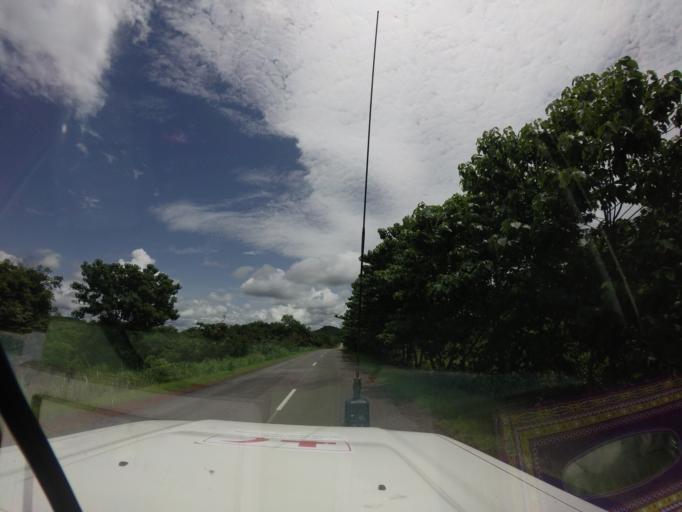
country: SL
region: Northern Province
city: Gberia Fotombu
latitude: 10.0604
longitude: -11.0250
